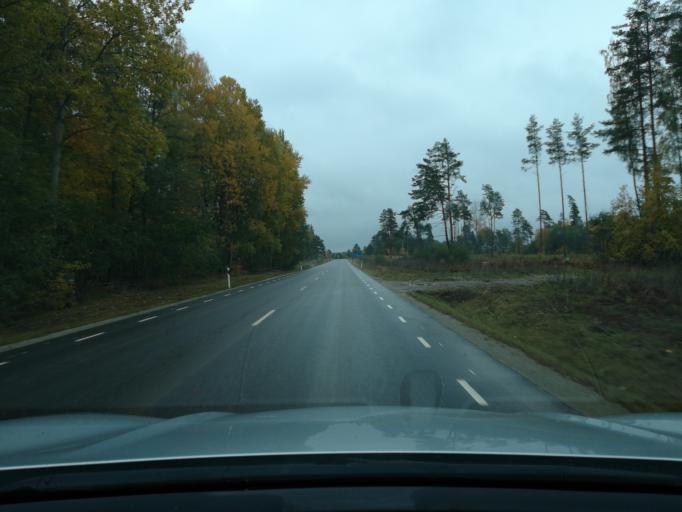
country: EE
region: Ida-Virumaa
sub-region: Johvi vald
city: Johvi
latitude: 59.2967
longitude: 27.4846
